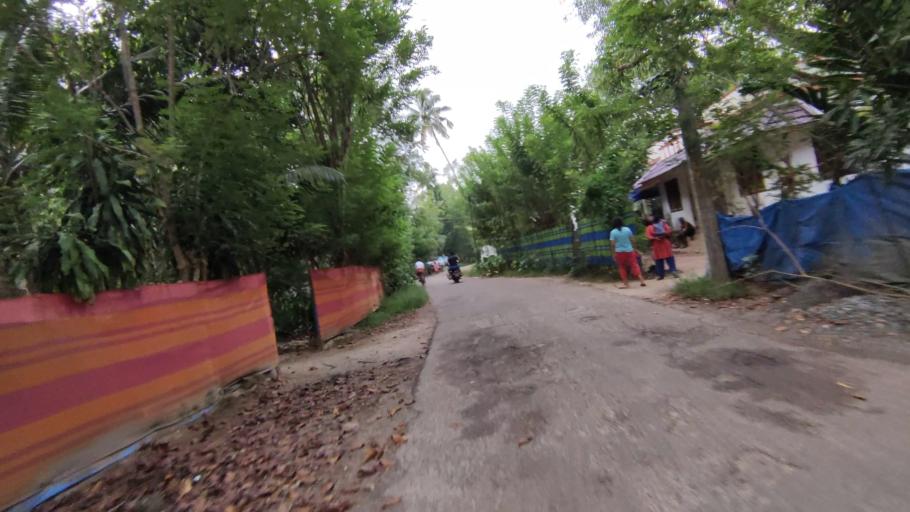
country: IN
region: Kerala
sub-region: Alappuzha
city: Shertallai
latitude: 9.6435
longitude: 76.3643
